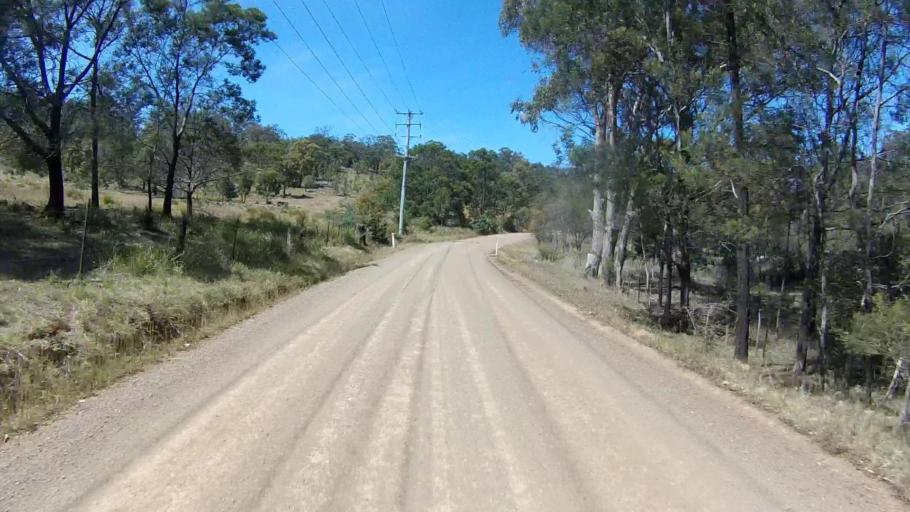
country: AU
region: Tasmania
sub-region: Sorell
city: Sorell
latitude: -42.7683
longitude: 147.6526
